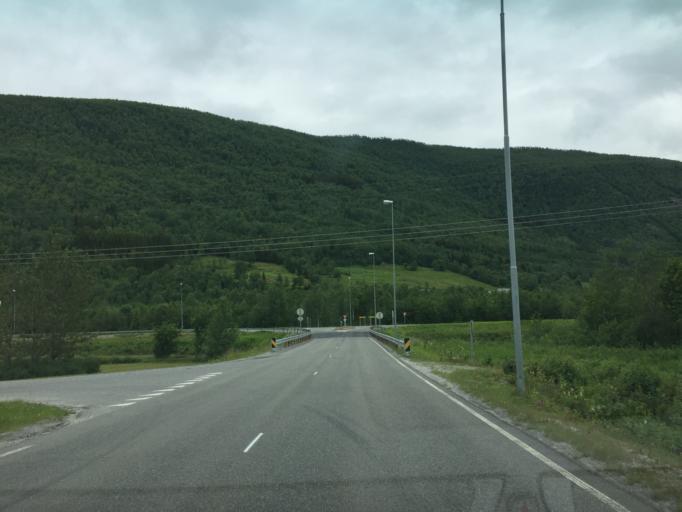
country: NO
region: Nordland
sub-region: Saltdal
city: Rognan
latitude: 67.0844
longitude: 15.3833
